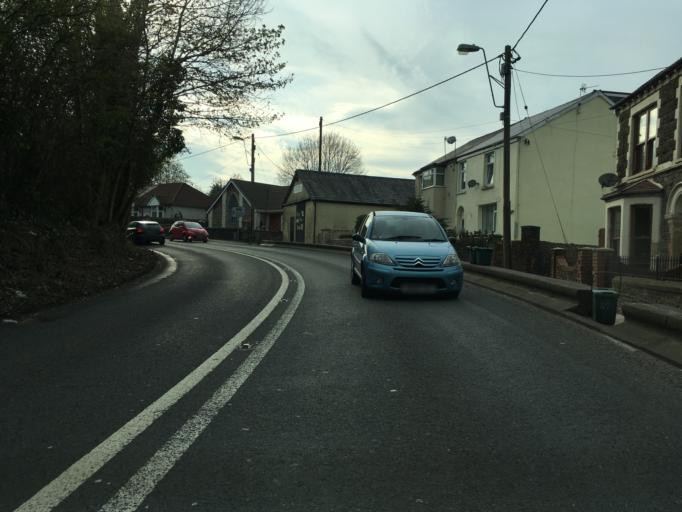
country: GB
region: Wales
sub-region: Caerphilly County Borough
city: Caerphilly
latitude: 51.5784
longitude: -3.2224
